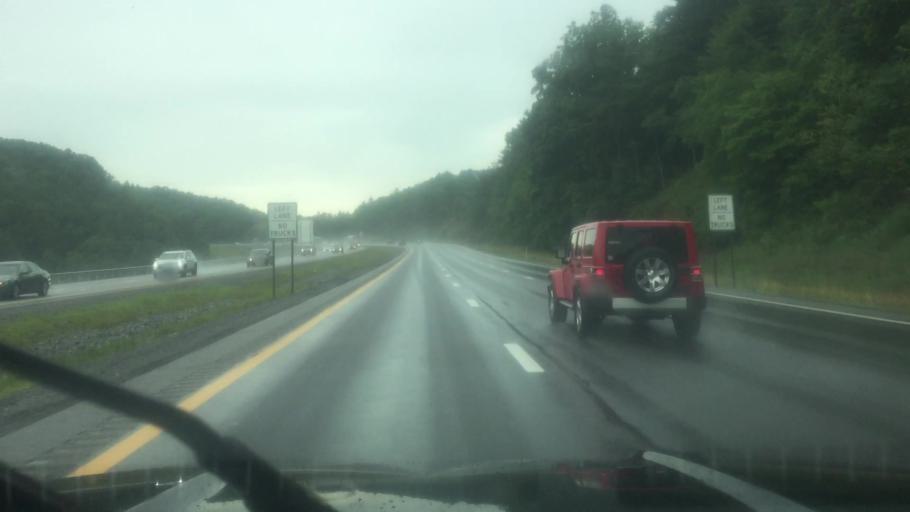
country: US
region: West Virginia
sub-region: Mercer County
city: Athens
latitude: 37.5211
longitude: -81.1113
